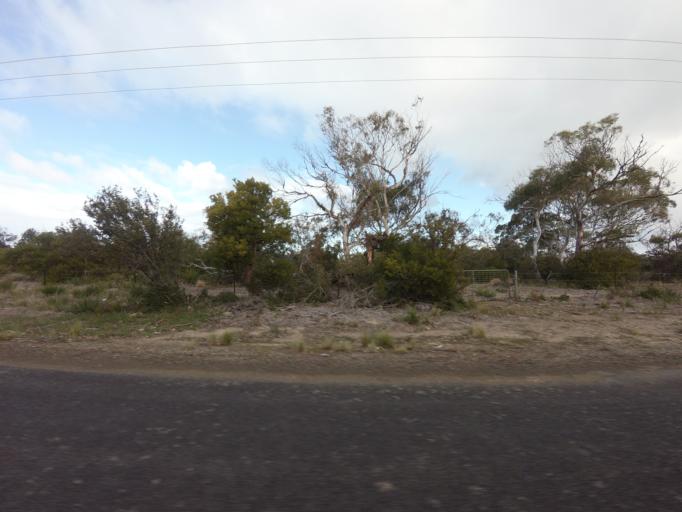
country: AU
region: Tasmania
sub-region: Break O'Day
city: St Helens
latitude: -42.0968
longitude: 148.0943
